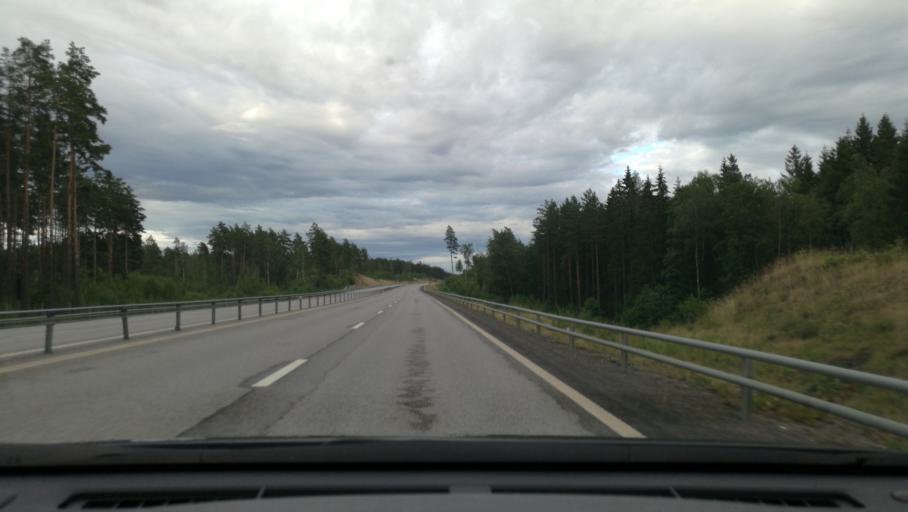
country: SE
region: OEstergoetland
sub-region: Norrkopings Kommun
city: Svartinge
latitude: 58.6679
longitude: 16.0047
